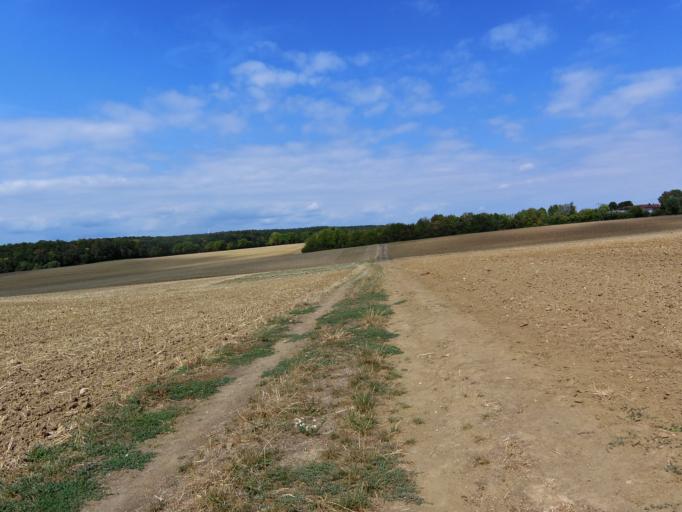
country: DE
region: Bavaria
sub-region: Regierungsbezirk Unterfranken
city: Gadheim
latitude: 49.8421
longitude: 9.9022
